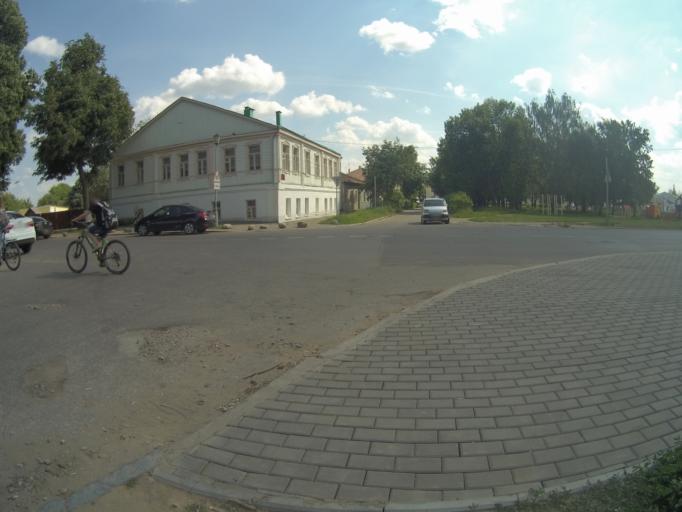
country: RU
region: Vladimir
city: Suzdal'
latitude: 56.4200
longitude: 40.4507
